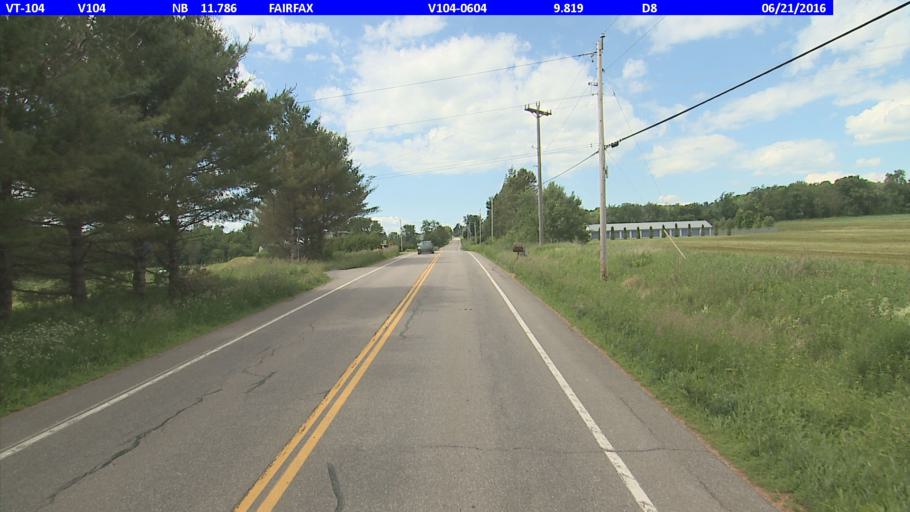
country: US
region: Vermont
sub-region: Franklin County
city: Saint Albans
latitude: 44.7256
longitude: -73.0444
